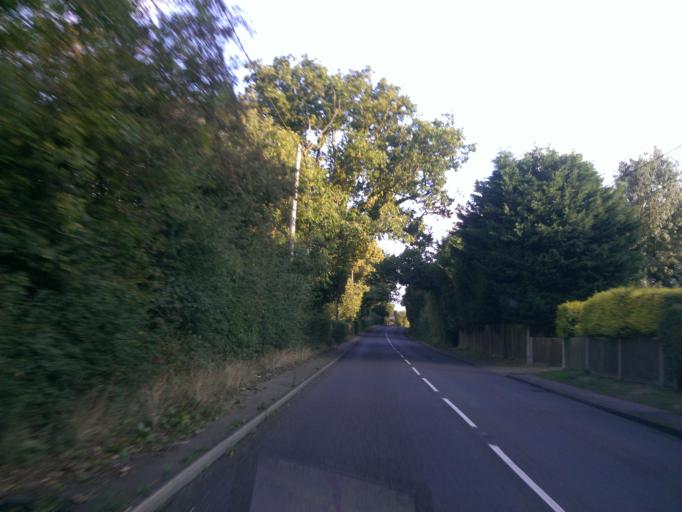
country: GB
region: England
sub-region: Essex
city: Sible Hedingham
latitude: 51.9433
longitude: 0.5904
